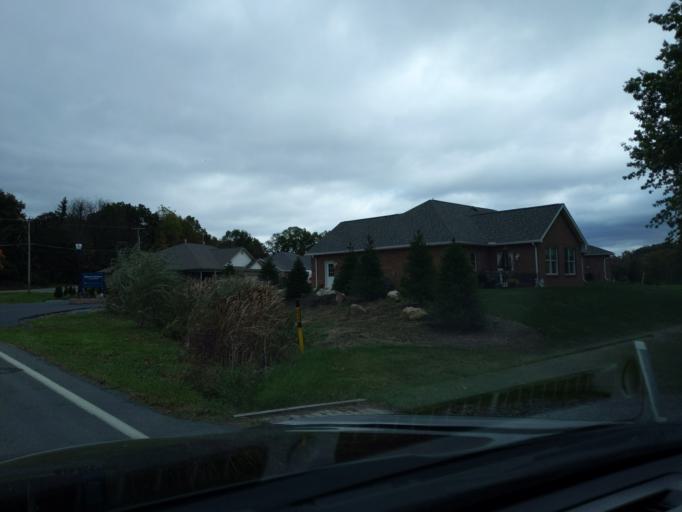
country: US
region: Pennsylvania
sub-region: Blair County
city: Hollidaysburg
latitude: 40.4394
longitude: -78.3891
